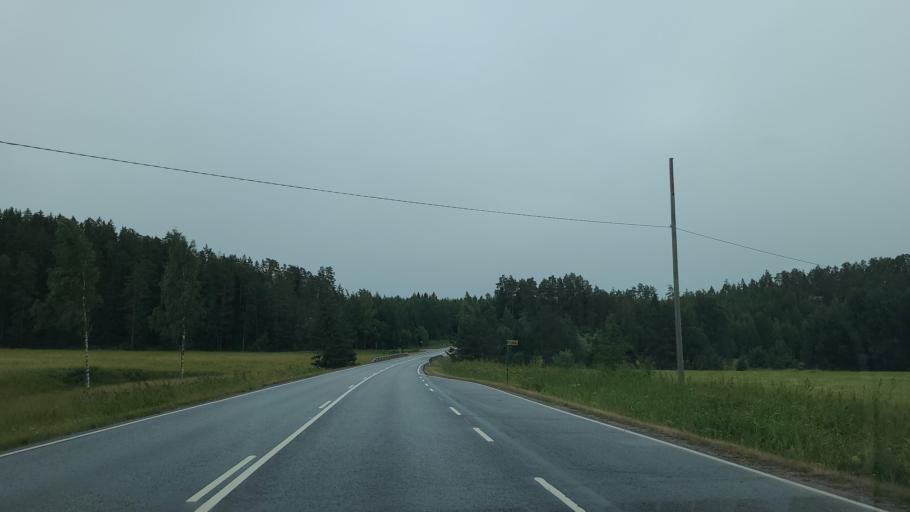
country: FI
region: Varsinais-Suomi
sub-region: Turku
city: Sauvo
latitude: 60.2745
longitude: 22.6694
